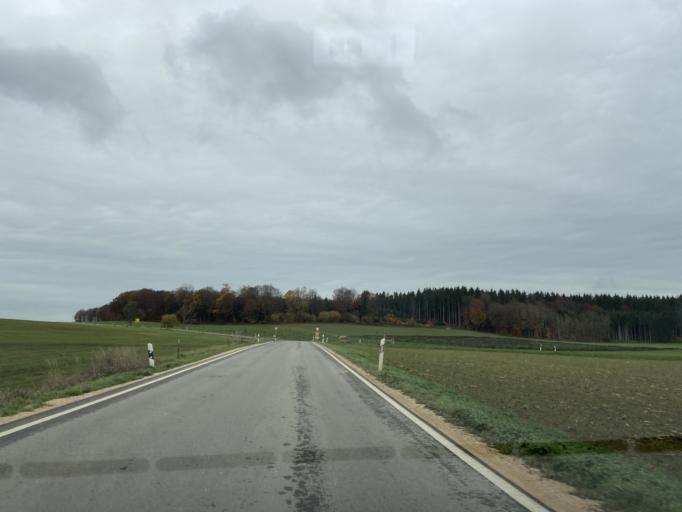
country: DE
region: Baden-Wuerttemberg
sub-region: Tuebingen Region
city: Wald
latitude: 47.9666
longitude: 9.1992
